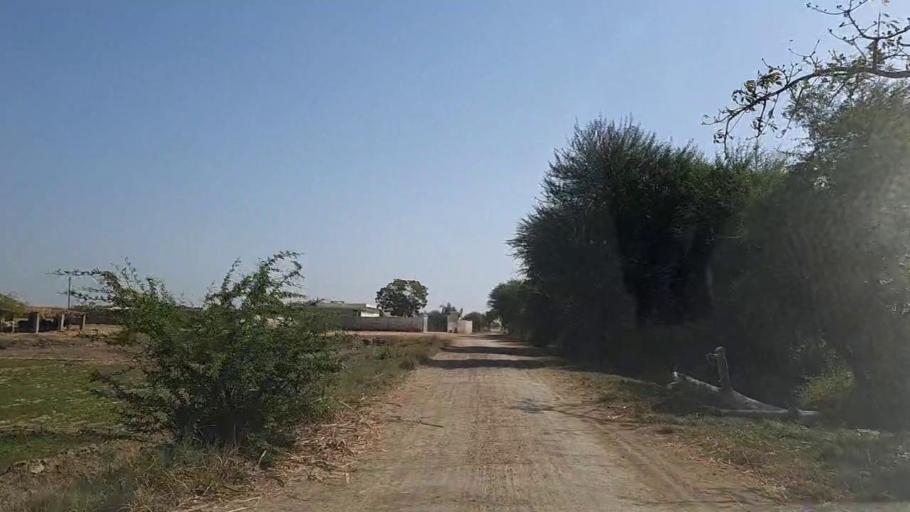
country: PK
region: Sindh
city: Samaro
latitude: 25.2715
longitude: 69.4048
